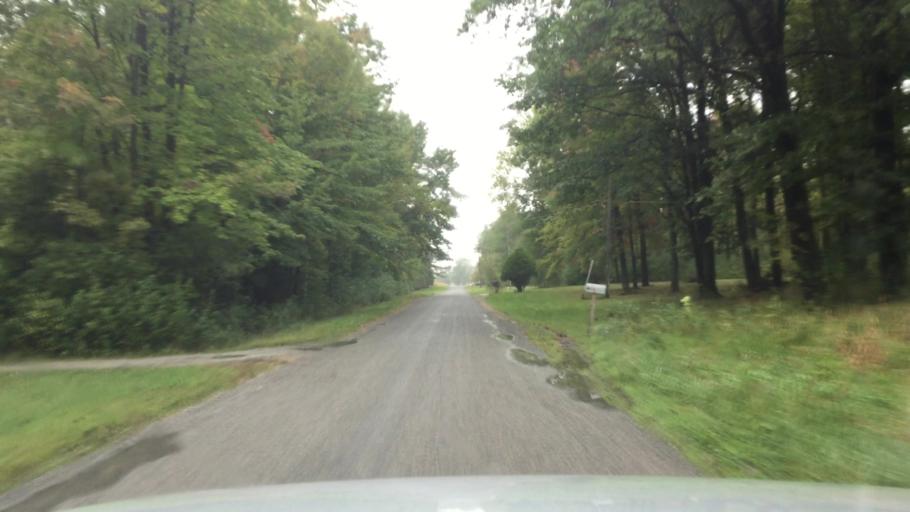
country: US
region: Michigan
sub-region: Saginaw County
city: Bridgeport
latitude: 43.3156
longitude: -83.8354
